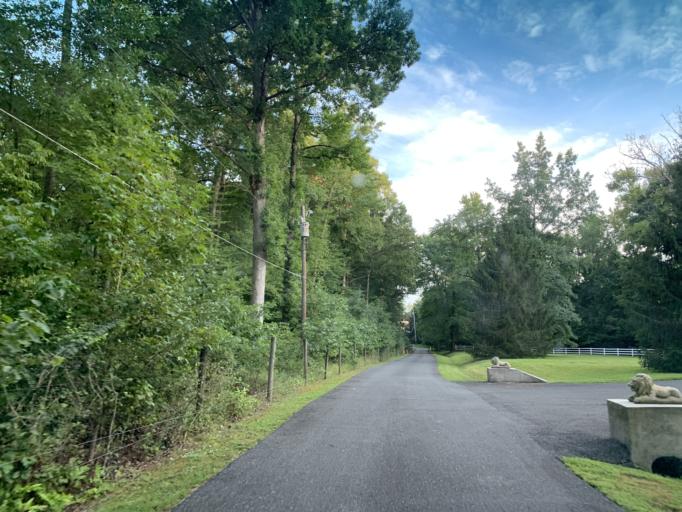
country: US
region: Maryland
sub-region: Harford County
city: Aberdeen
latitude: 39.5236
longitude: -76.1588
